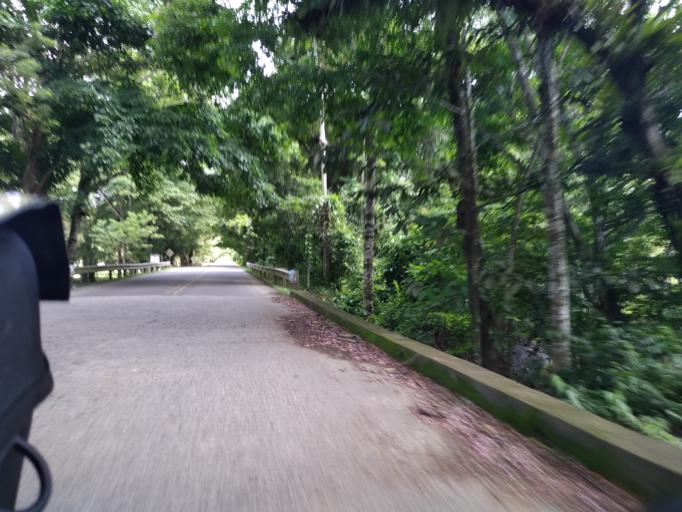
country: CO
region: Santander
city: Puerto Parra
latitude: 6.5193
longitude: -74.0763
